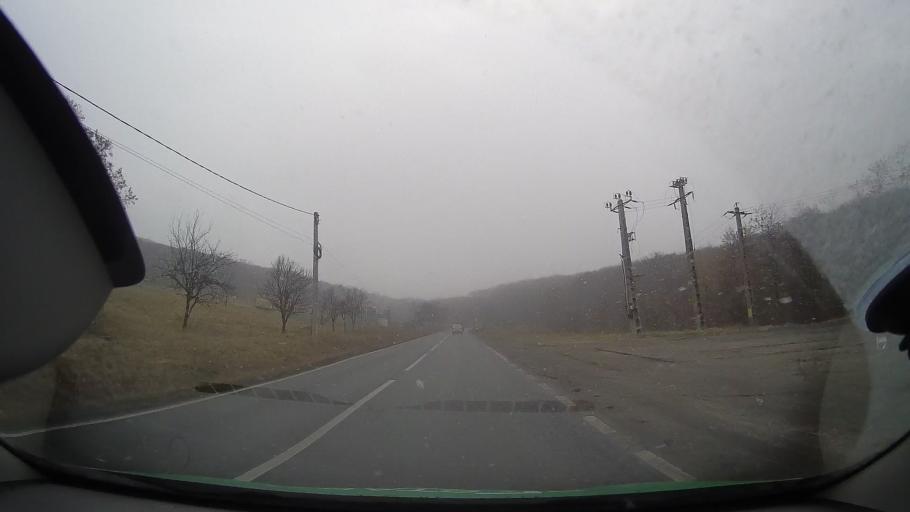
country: RO
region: Sibiu
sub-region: Comuna Blajel
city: Blajel
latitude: 46.1929
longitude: 24.3243
